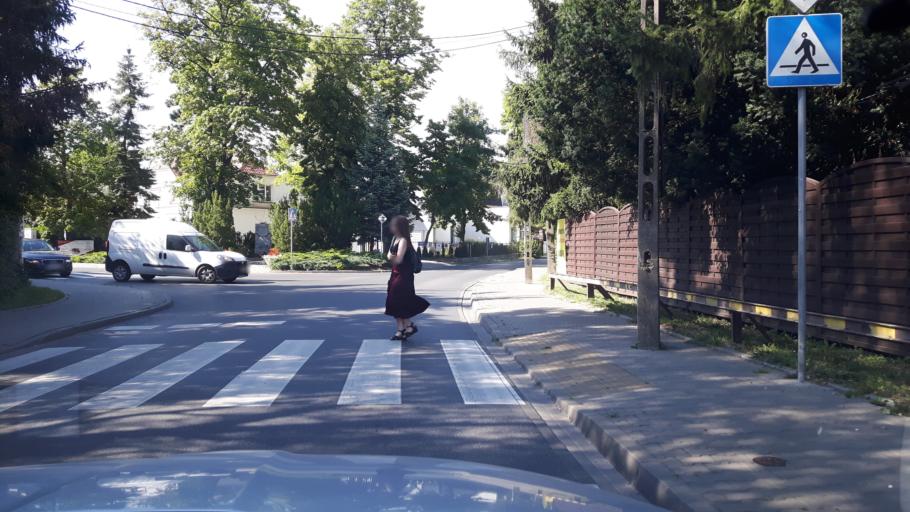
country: PL
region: Masovian Voivodeship
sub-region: Powiat pruszkowski
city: Nowe Grocholice
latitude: 52.1819
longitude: 20.9041
